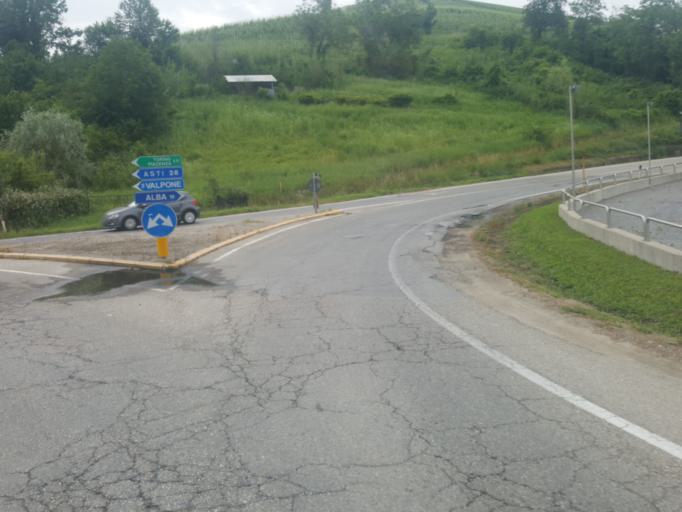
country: IT
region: Piedmont
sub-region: Provincia di Cuneo
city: Canale
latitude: 44.7929
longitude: 8.0020
